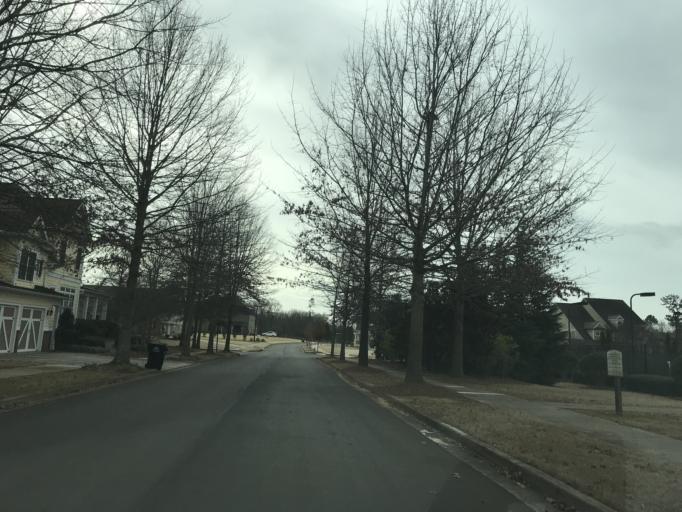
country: US
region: Georgia
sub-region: Cherokee County
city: Canton
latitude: 34.2040
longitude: -84.3984
